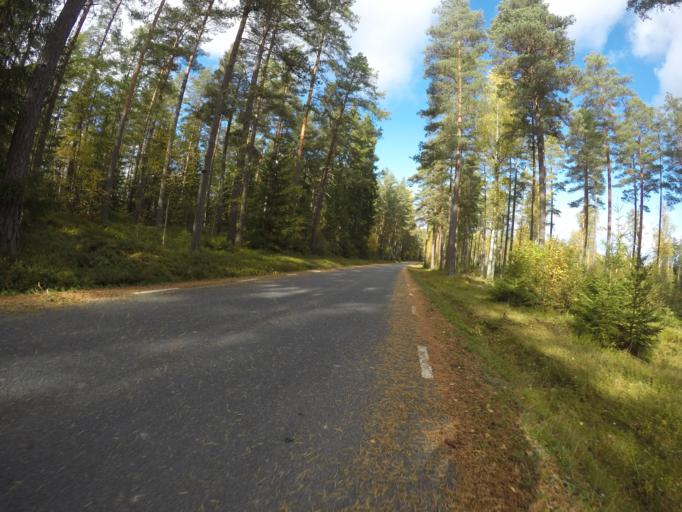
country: SE
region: Vaestmanland
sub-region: Kungsors Kommun
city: Kungsoer
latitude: 59.3182
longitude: 16.1156
